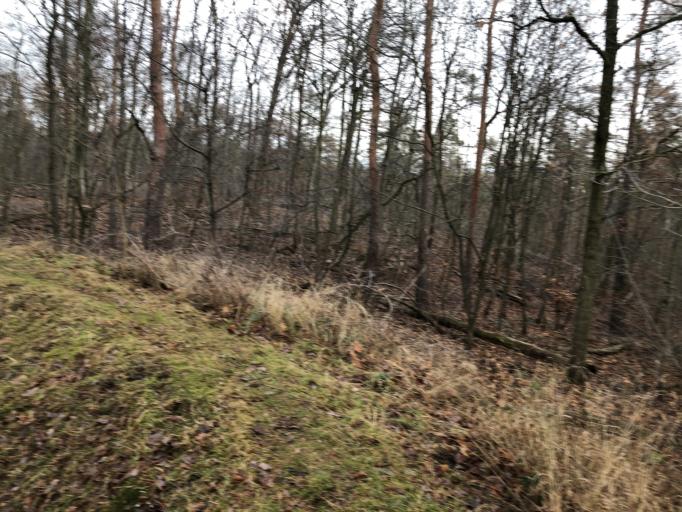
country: DE
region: Saxony-Anhalt
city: Halle Neustadt
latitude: 51.4979
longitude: 11.9011
